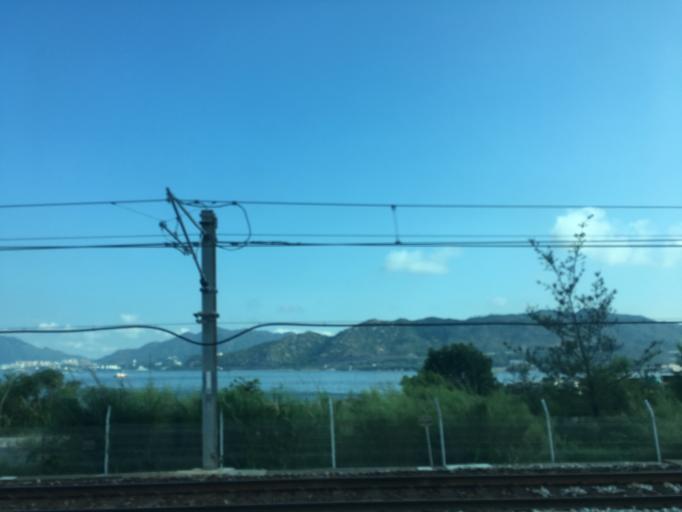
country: HK
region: Tsuen Wan
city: Tsuen Wan
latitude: 22.3388
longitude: 114.0390
